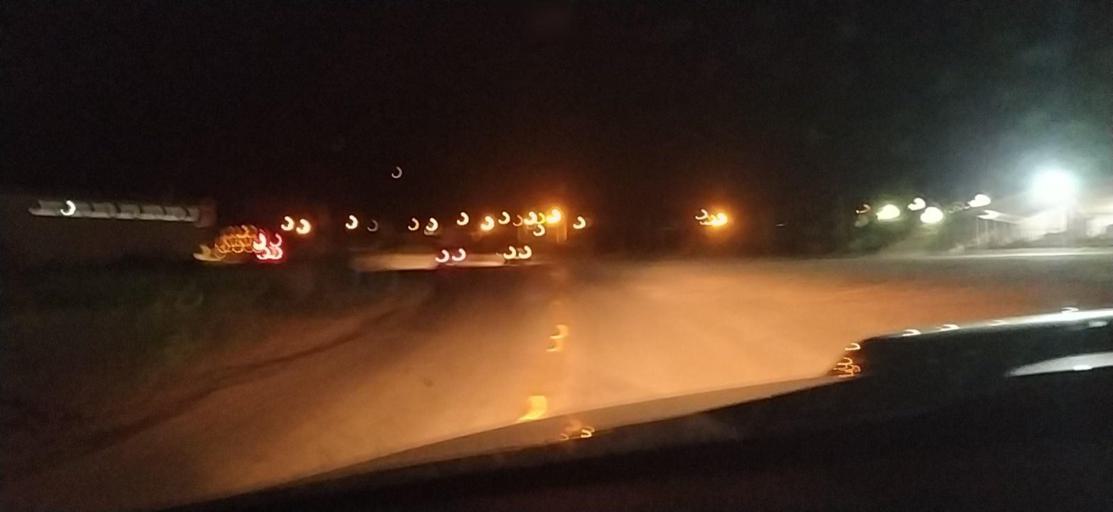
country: BR
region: Minas Gerais
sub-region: Monte Azul
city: Monte Azul
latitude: -15.1503
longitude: -42.8618
